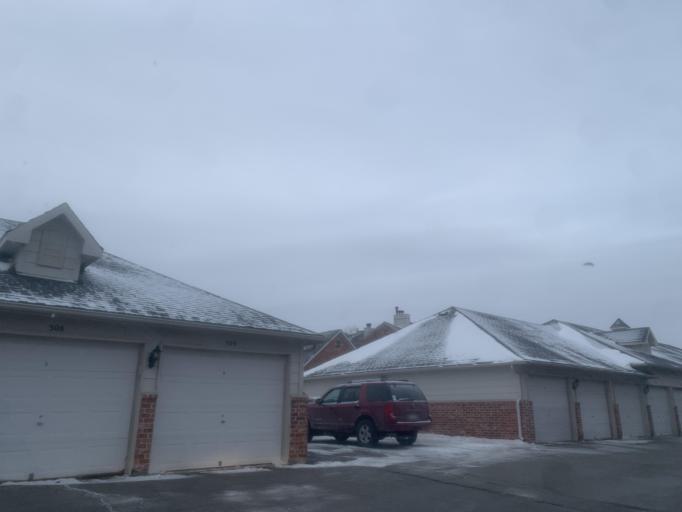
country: US
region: Nebraska
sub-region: Douglas County
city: Ralston
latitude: 41.2715
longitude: -96.0878
